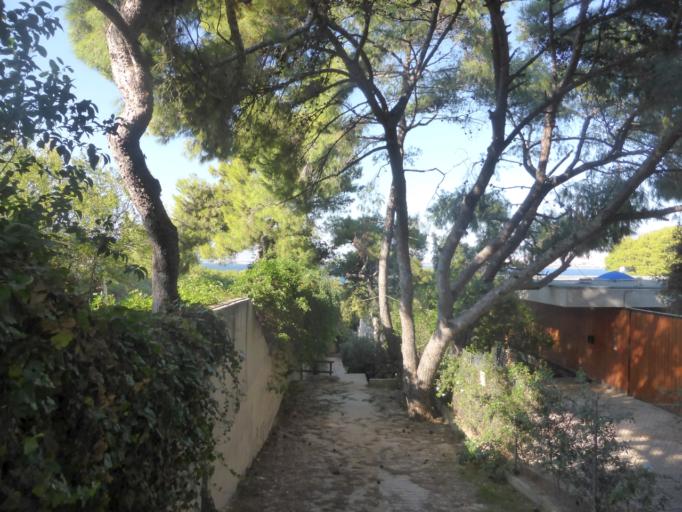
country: GR
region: Attica
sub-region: Nomarchia Anatolikis Attikis
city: Vouliagmeni
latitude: 37.8158
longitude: 23.7619
